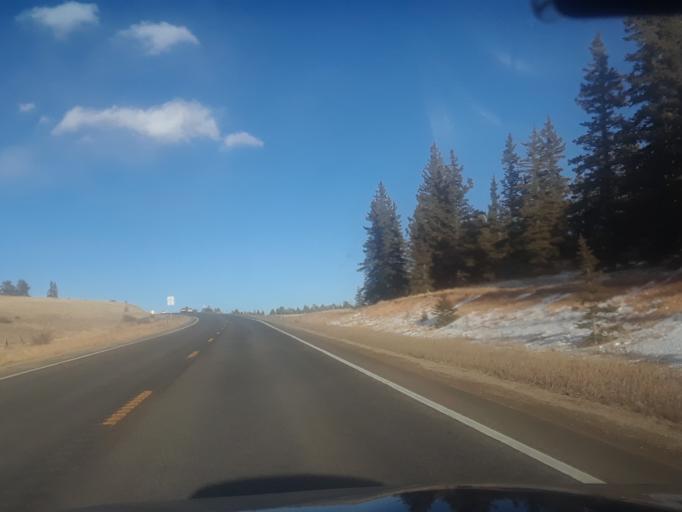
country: US
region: Colorado
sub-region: Chaffee County
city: Buena Vista
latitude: 38.9068
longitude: -105.9820
